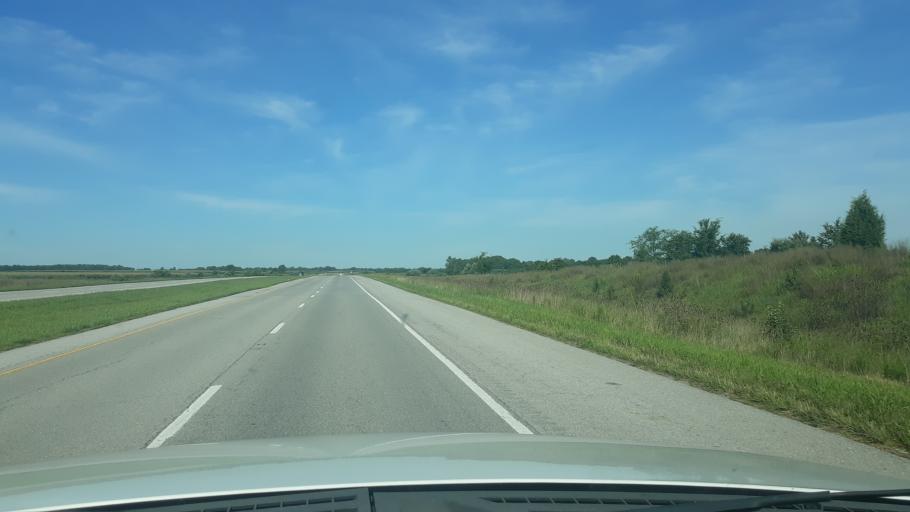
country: US
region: Illinois
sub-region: Saline County
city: Harrisburg
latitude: 37.7318
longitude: -88.5809
